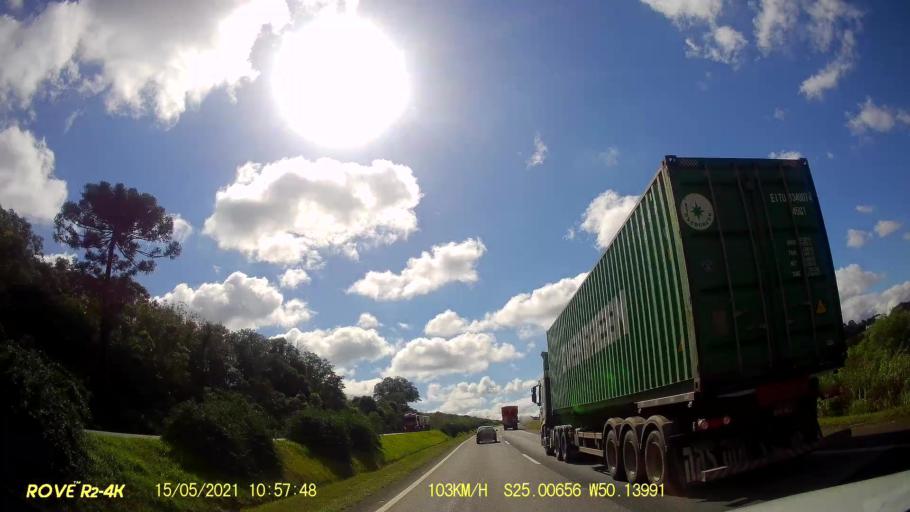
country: BR
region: Parana
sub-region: Carambei
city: Carambei
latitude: -25.0063
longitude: -50.1399
